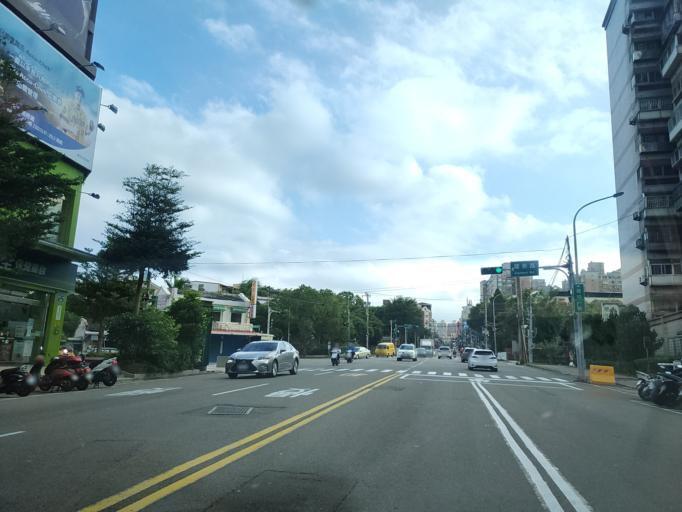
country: TW
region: Taiwan
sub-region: Hsinchu
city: Hsinchu
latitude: 24.8013
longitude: 120.9969
